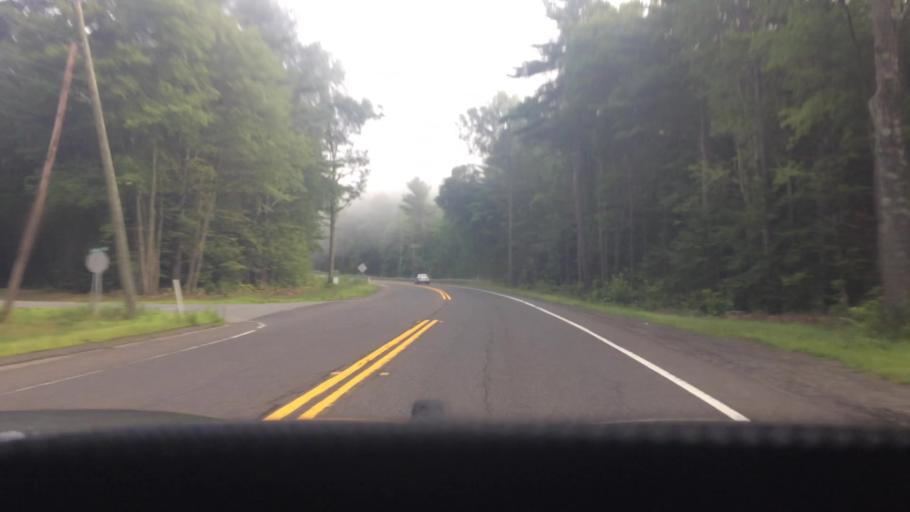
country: US
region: Massachusetts
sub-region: Franklin County
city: Millers Falls
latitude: 42.5925
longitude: -72.4906
